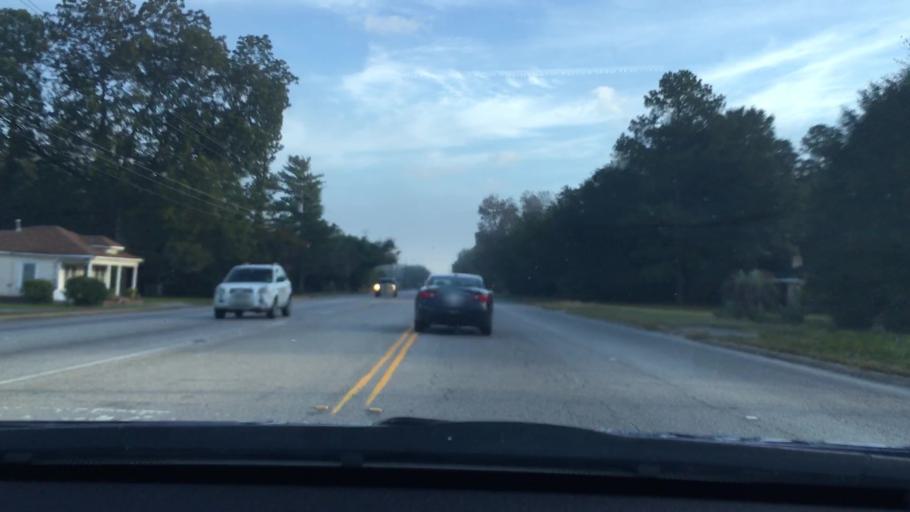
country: US
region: South Carolina
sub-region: Sumter County
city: South Sumter
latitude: 33.8885
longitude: -80.3453
